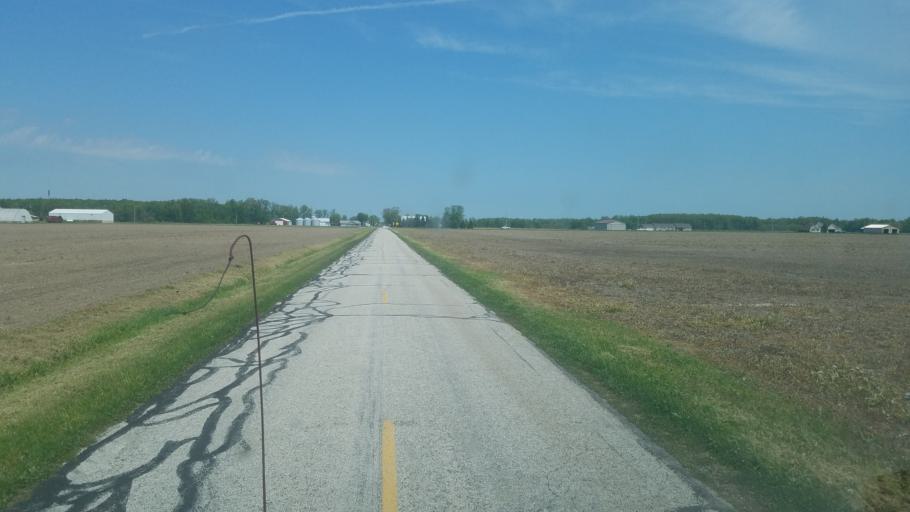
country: US
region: Ohio
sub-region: Ottawa County
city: Oak Harbor
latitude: 41.4687
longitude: -83.2018
